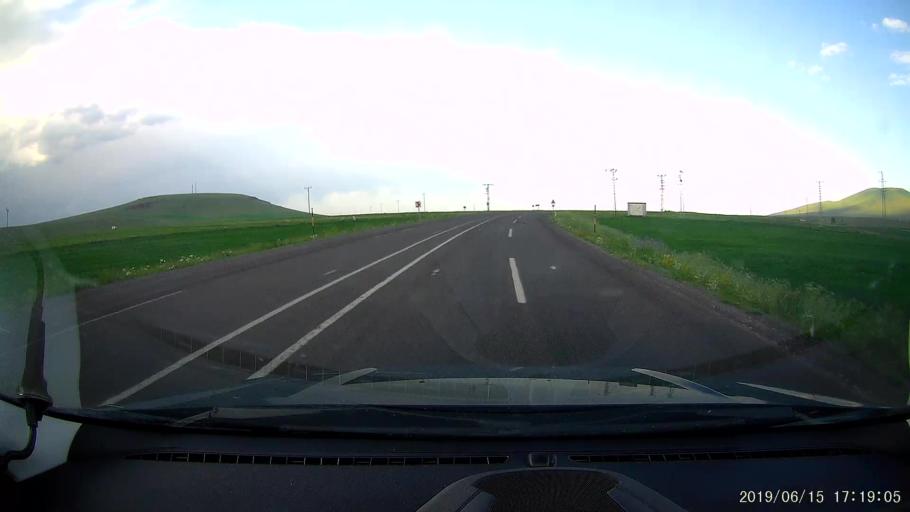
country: TR
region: Kars
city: Kars
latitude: 40.6159
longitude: 43.2712
